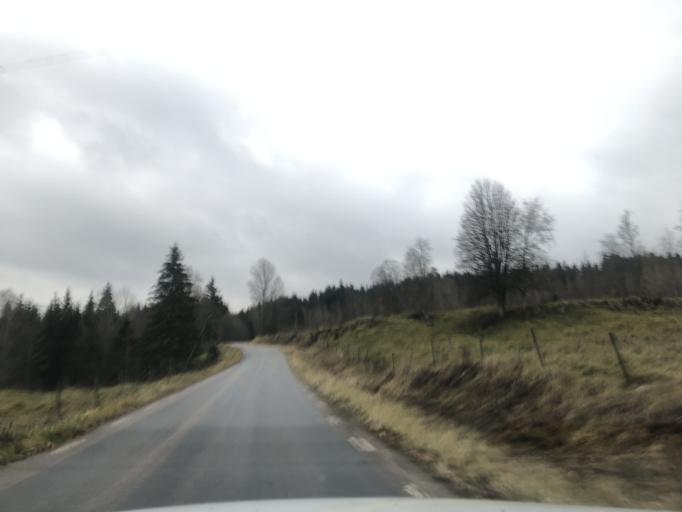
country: SE
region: Vaestra Goetaland
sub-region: Ulricehamns Kommun
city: Ulricehamn
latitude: 57.8803
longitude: 13.5187
